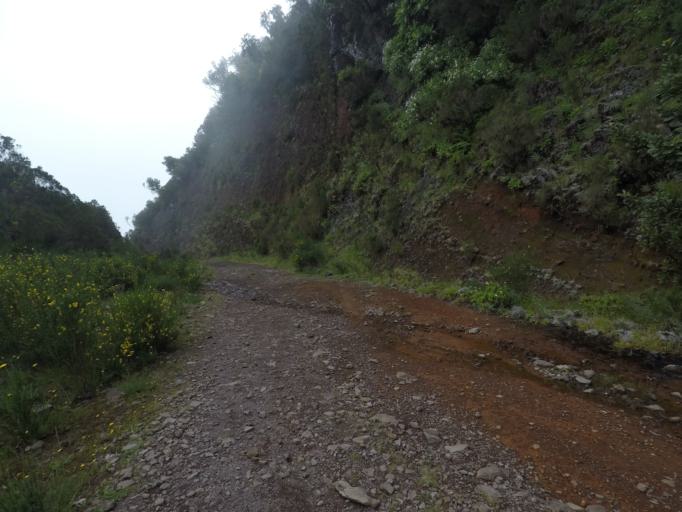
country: PT
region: Madeira
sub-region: Sao Vicente
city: Sao Vicente
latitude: 32.7683
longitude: -17.0670
